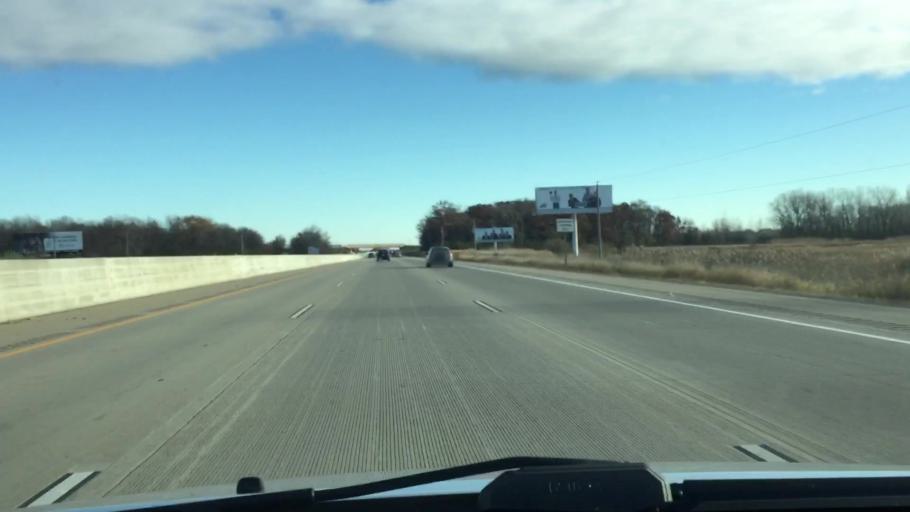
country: US
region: Wisconsin
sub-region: Winnebago County
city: Oshkosh
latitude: 44.1067
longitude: -88.5289
